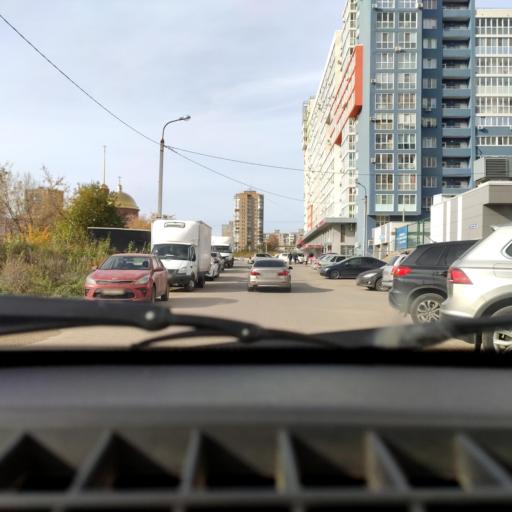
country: RU
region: Bashkortostan
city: Ufa
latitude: 54.7632
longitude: 56.0304
